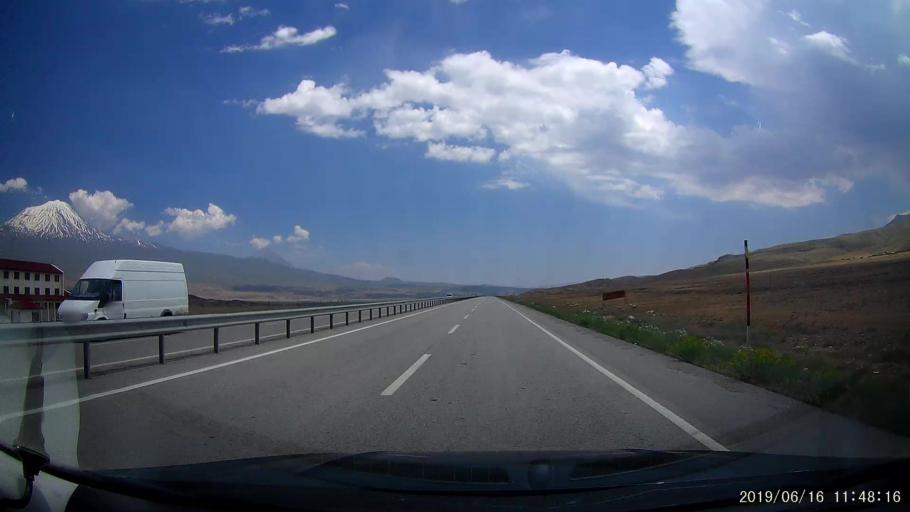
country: TR
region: Agri
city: Dogubayazit
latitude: 39.5581
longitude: 44.1406
